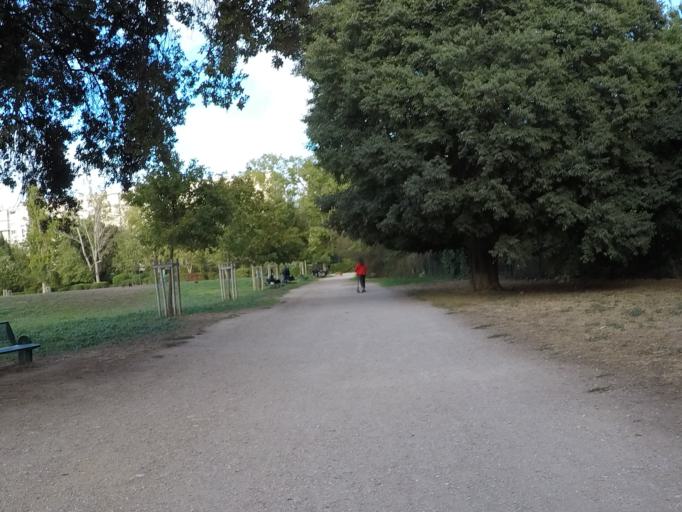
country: FR
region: Provence-Alpes-Cote d'Azur
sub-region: Departement des Bouches-du-Rhone
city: Marseille 08
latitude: 43.2630
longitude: 5.3850
